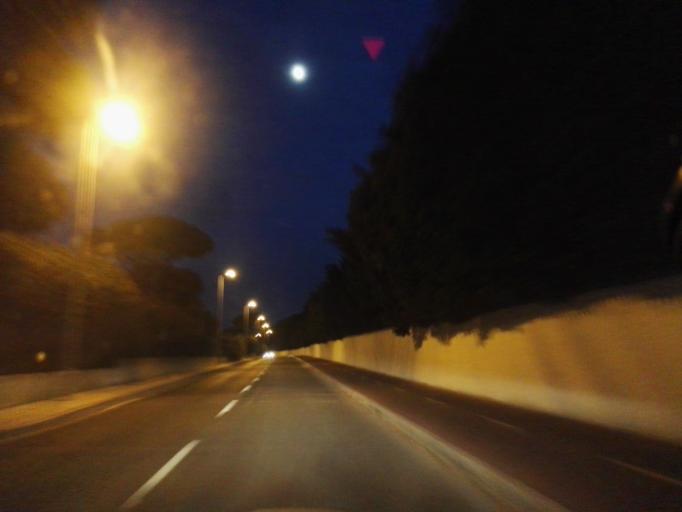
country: PT
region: Lisbon
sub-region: Cascais
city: Cascais
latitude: 38.7192
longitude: -9.4648
